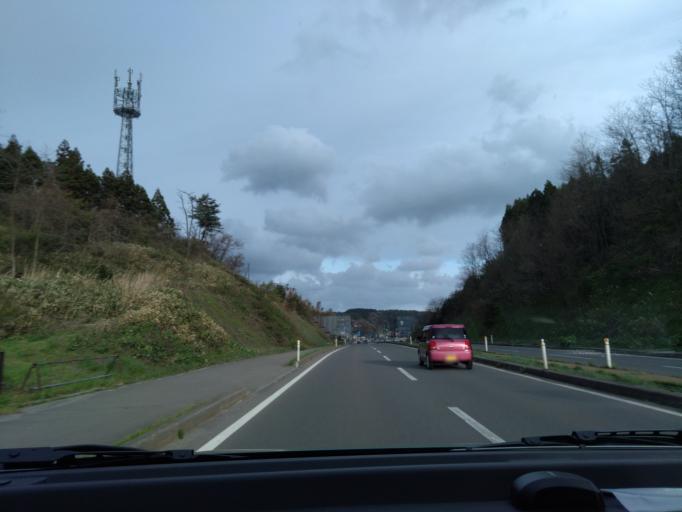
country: JP
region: Akita
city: Akita
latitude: 39.7502
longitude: 140.1235
